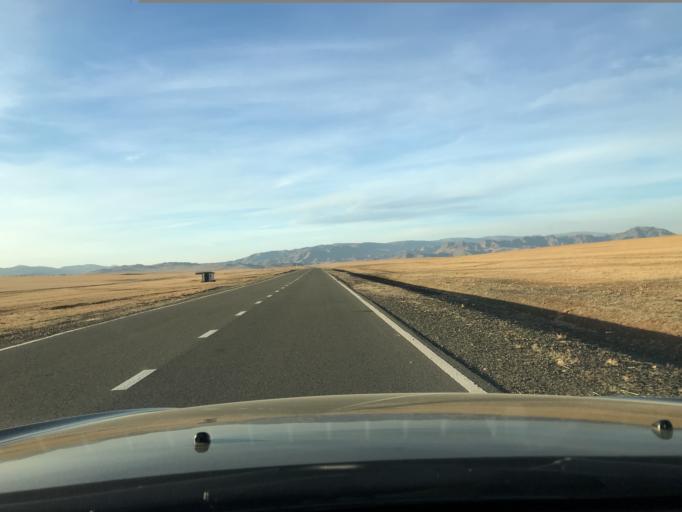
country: MN
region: Central Aimak
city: Arhust
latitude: 47.7413
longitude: 107.4614
